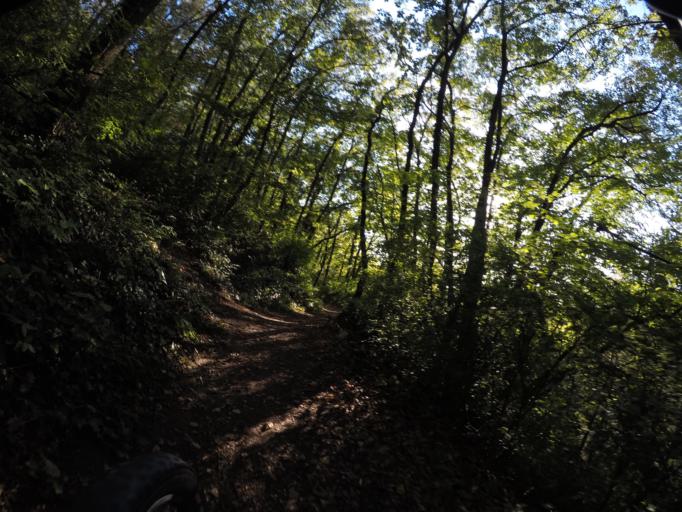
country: AT
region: Lower Austria
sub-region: Politischer Bezirk Bruck an der Leitha
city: Mannersdorf am Leithagebirge
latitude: 47.9673
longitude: 16.6017
